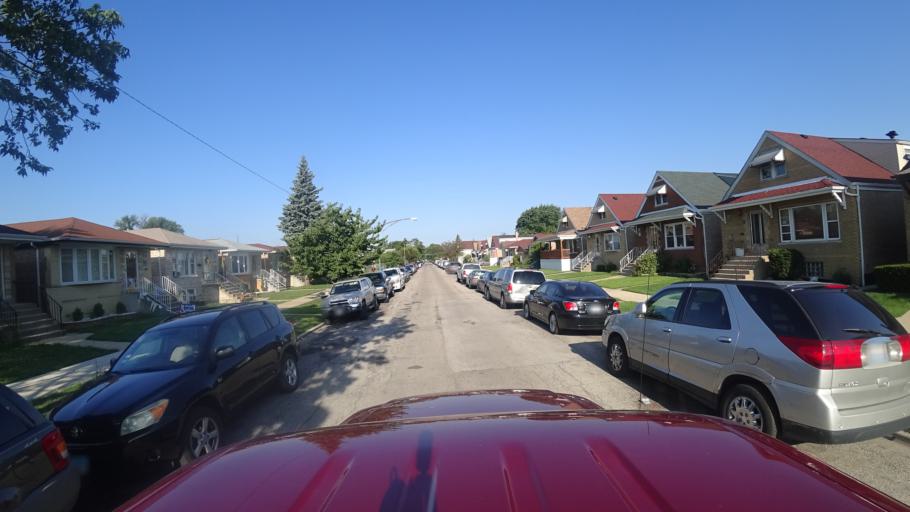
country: US
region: Illinois
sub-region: Cook County
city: Hometown
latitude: 41.7924
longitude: -87.7137
